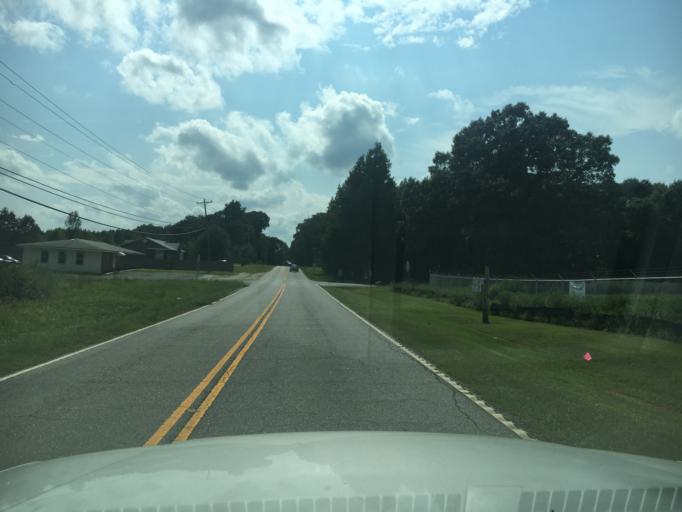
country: US
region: South Carolina
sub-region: Anderson County
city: Belton
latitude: 34.5324
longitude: -82.4708
